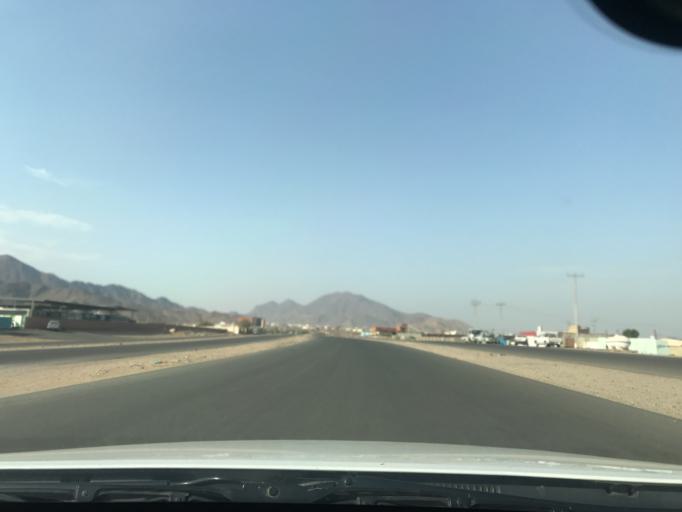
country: SA
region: Makkah
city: Al Jumum
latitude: 21.4446
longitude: 39.5184
